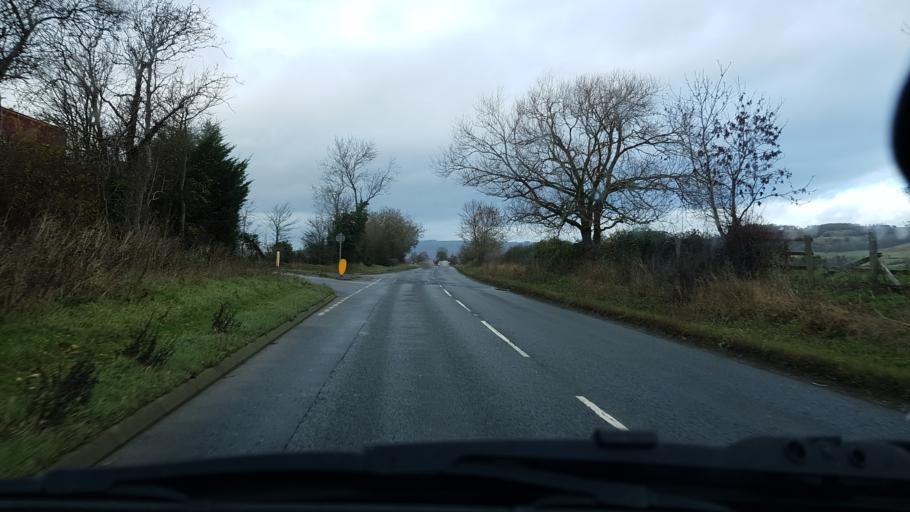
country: GB
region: England
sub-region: Gloucestershire
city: Gotherington
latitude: 51.9694
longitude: -2.0706
